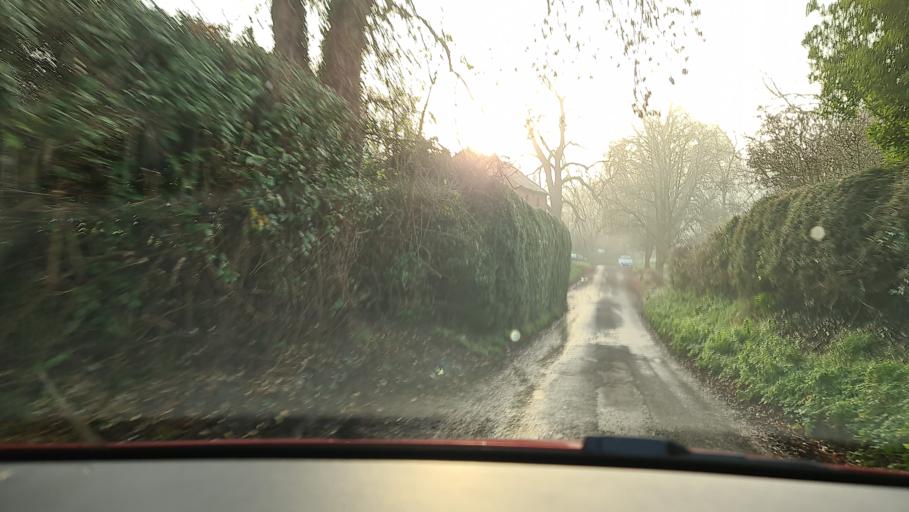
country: GB
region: England
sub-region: Buckinghamshire
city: Haddenham
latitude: 51.8052
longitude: -0.9392
